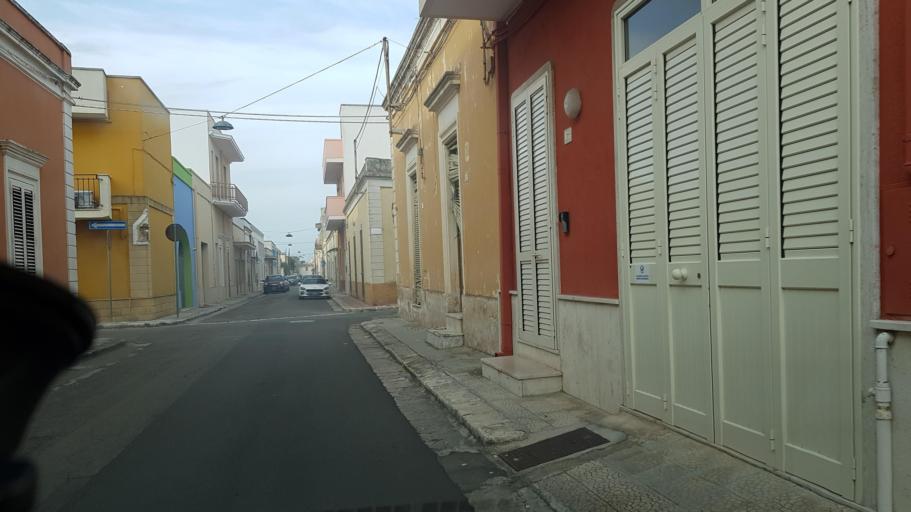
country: IT
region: Apulia
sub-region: Provincia di Lecce
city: Trepuzzi
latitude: 40.4030
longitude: 18.0770
